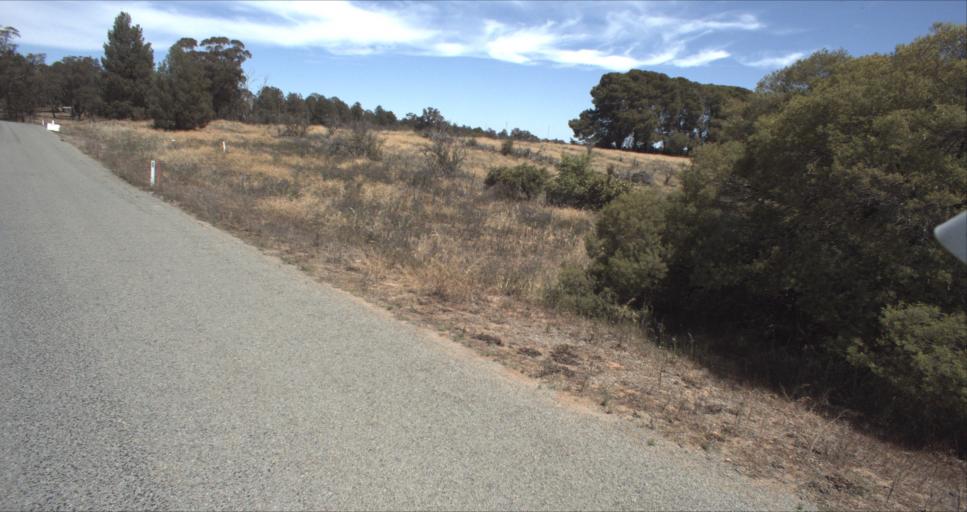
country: AU
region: New South Wales
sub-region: Leeton
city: Leeton
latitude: -34.6683
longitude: 146.4466
